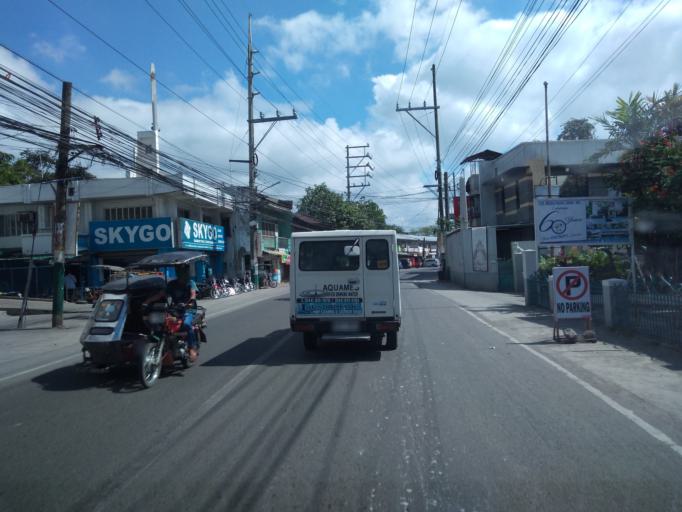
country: PH
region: Central Luzon
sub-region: Province of Bulacan
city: Santa Maria
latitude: 14.8171
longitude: 120.9524
